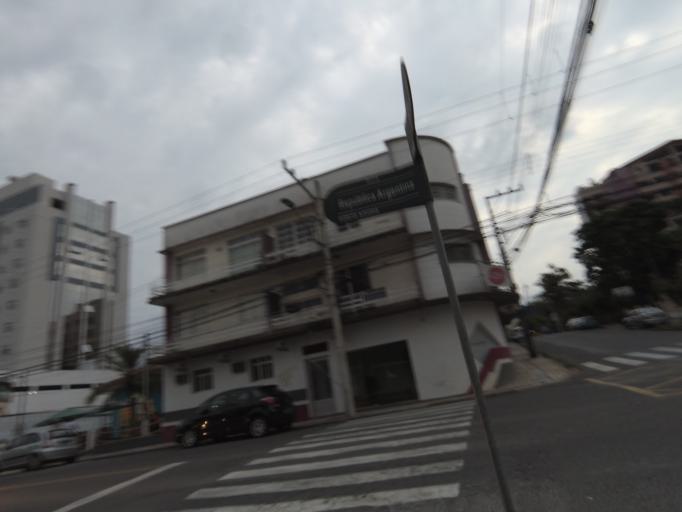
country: BR
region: Santa Catarina
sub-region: Blumenau
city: Blumenau
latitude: -26.9164
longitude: -49.0627
